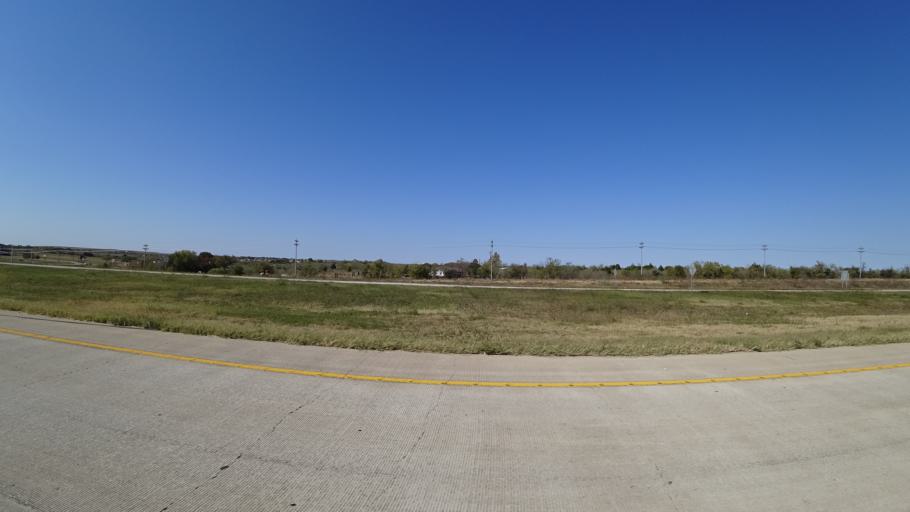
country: US
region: Texas
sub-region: Travis County
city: Manor
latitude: 30.3549
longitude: -97.5903
